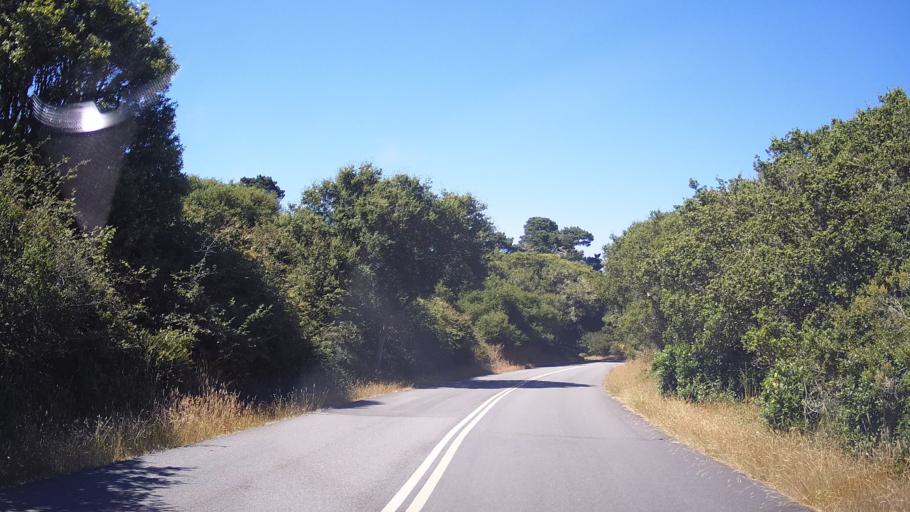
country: US
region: California
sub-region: Marin County
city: Inverness
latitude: 38.1254
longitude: -122.9020
